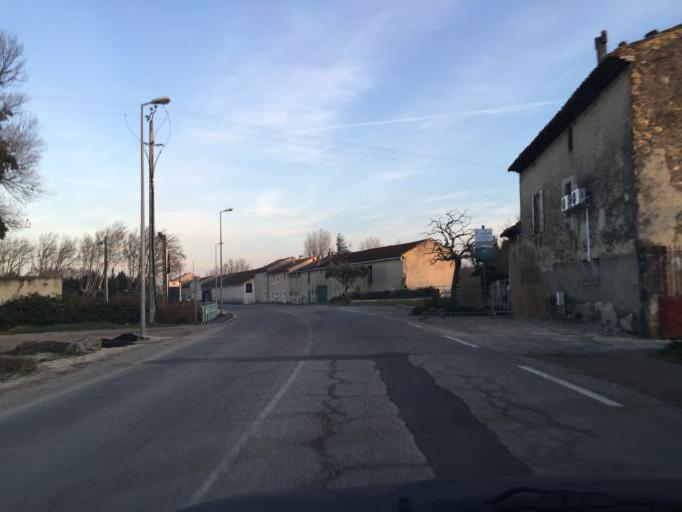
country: FR
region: Provence-Alpes-Cote d'Azur
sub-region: Departement du Vaucluse
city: Jonquieres
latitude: 44.1157
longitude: 4.8899
